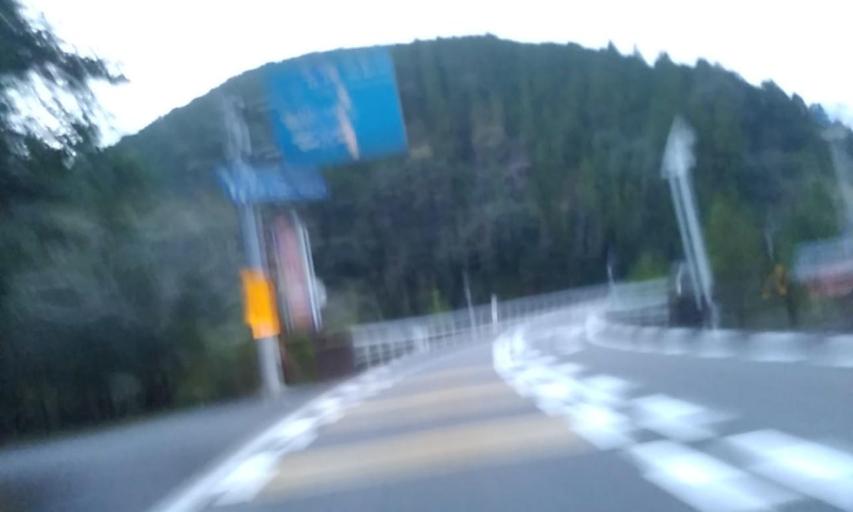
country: JP
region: Wakayama
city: Shingu
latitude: 33.7428
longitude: 135.9381
